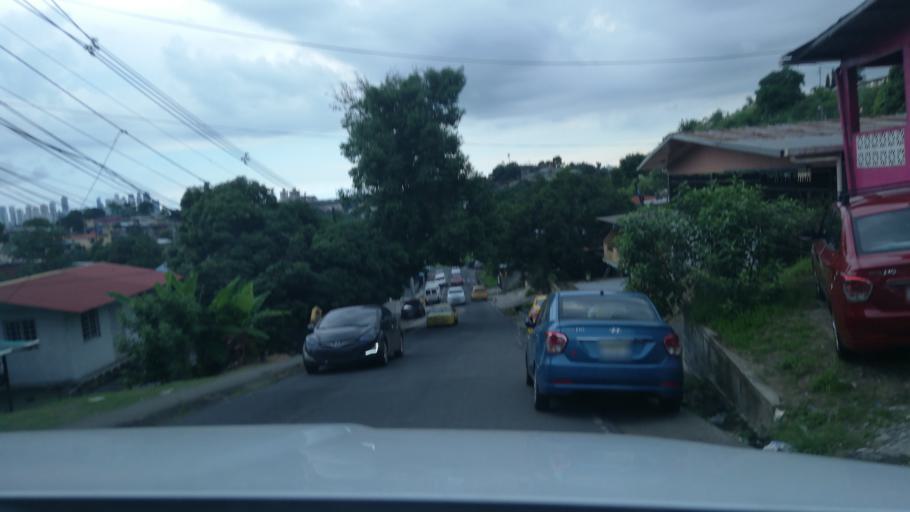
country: PA
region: Panama
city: San Miguelito
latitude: 9.0504
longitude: -79.4928
